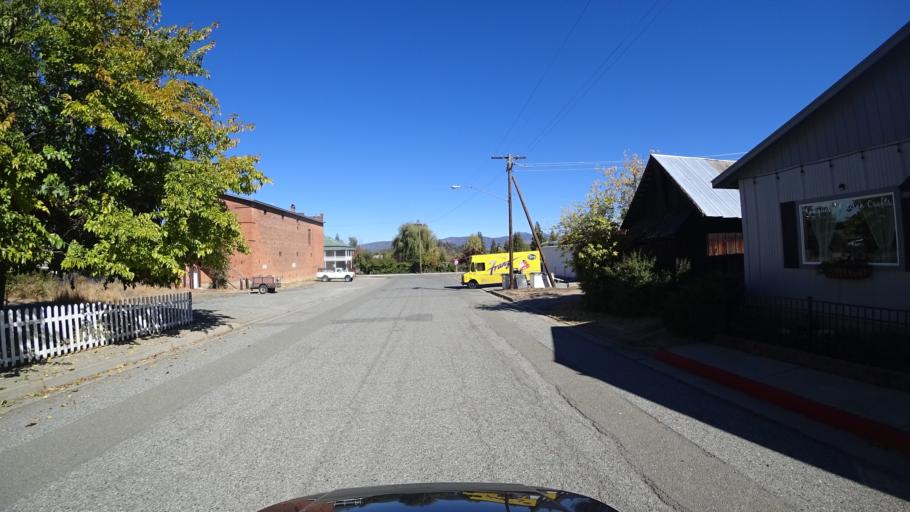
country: US
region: California
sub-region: Siskiyou County
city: Yreka
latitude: 41.4572
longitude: -122.8944
